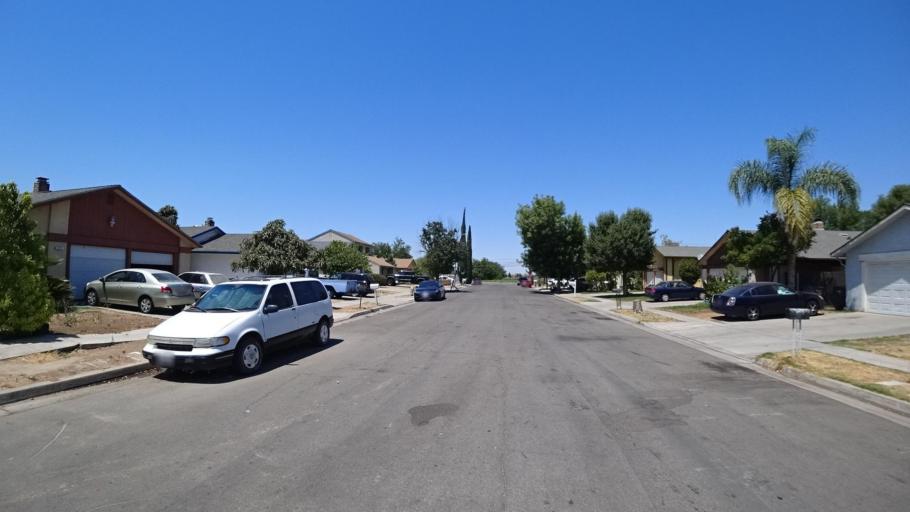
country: US
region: California
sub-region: Fresno County
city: Fresno
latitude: 36.7209
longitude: -119.7354
